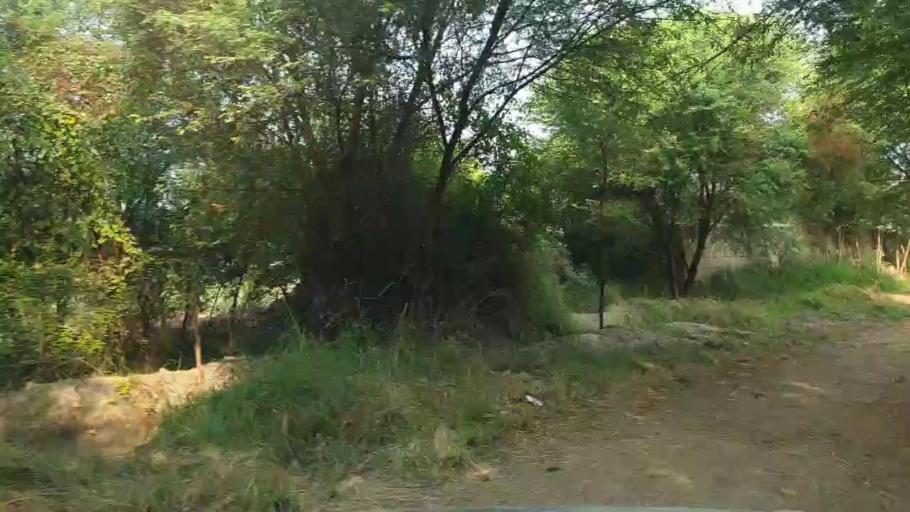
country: PK
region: Sindh
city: Tando Jam
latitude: 25.3337
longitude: 68.5145
